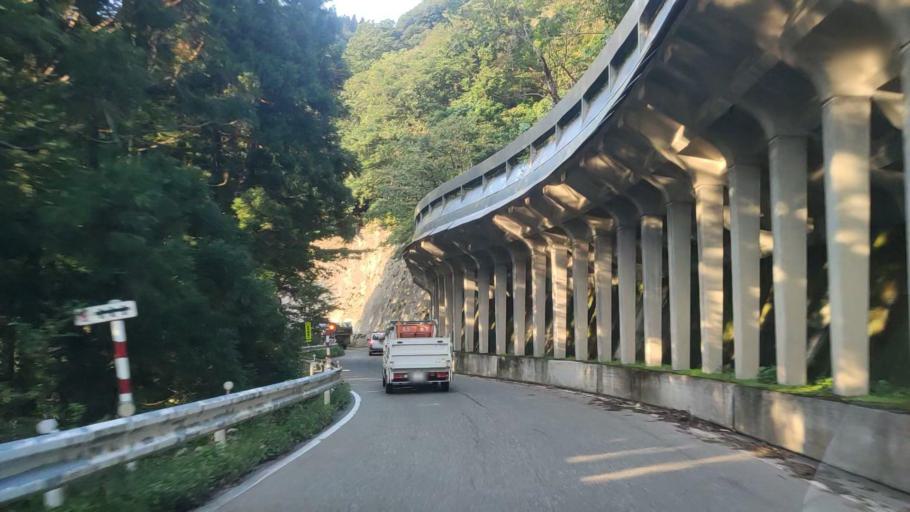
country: JP
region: Toyama
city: Nanto-shi
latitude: 36.5563
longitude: 137.0112
